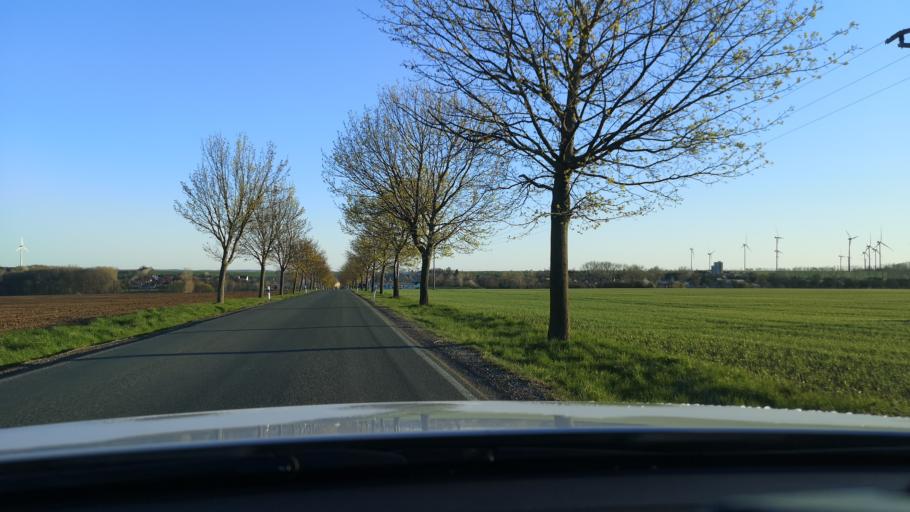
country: DE
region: Thuringia
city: Hainichen
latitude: 51.0209
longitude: 11.5993
